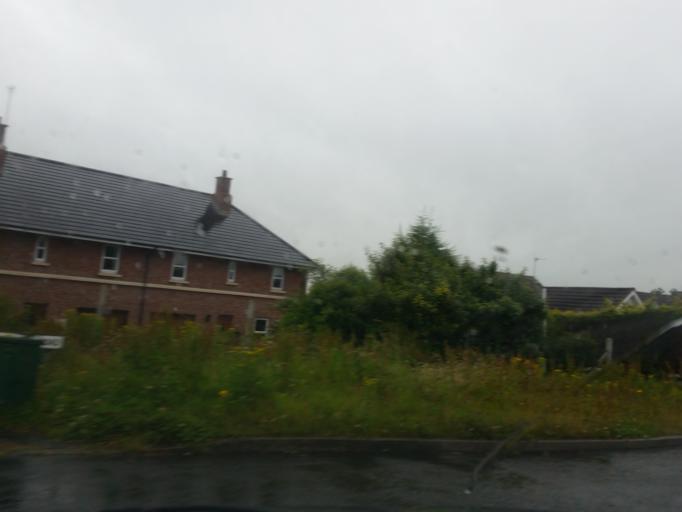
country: GB
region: Northern Ireland
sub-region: North Down District
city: Bangor
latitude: 54.6534
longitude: -5.6391
